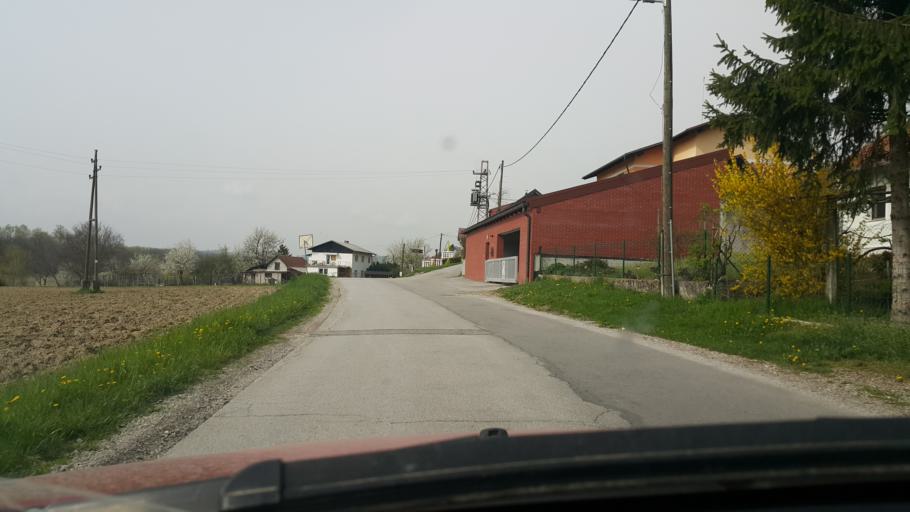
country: SI
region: Duplek
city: Zgornji Duplek
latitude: 46.5212
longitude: 15.7167
